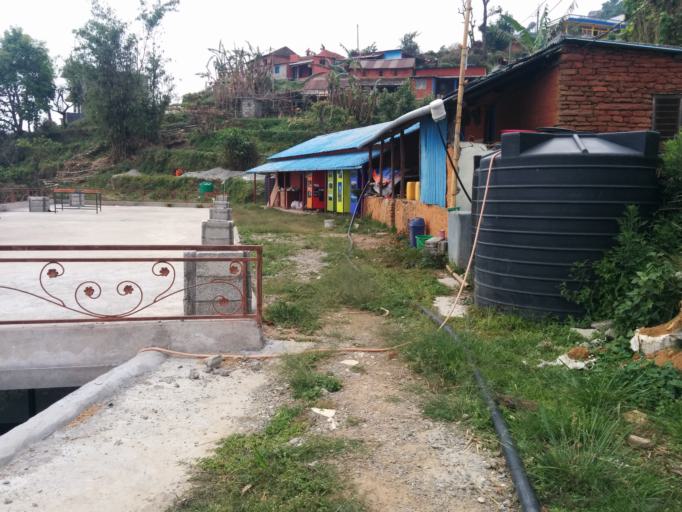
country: NP
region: Western Region
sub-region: Gandaki Zone
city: Pokhara
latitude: 28.2451
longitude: 83.9518
